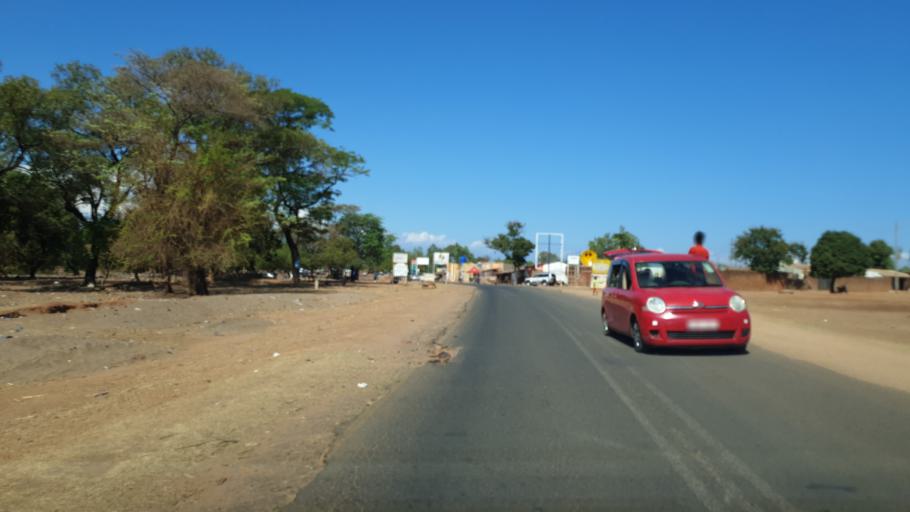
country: MW
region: Central Region
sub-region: Salima District
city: Salima
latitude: -13.7313
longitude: 34.6126
